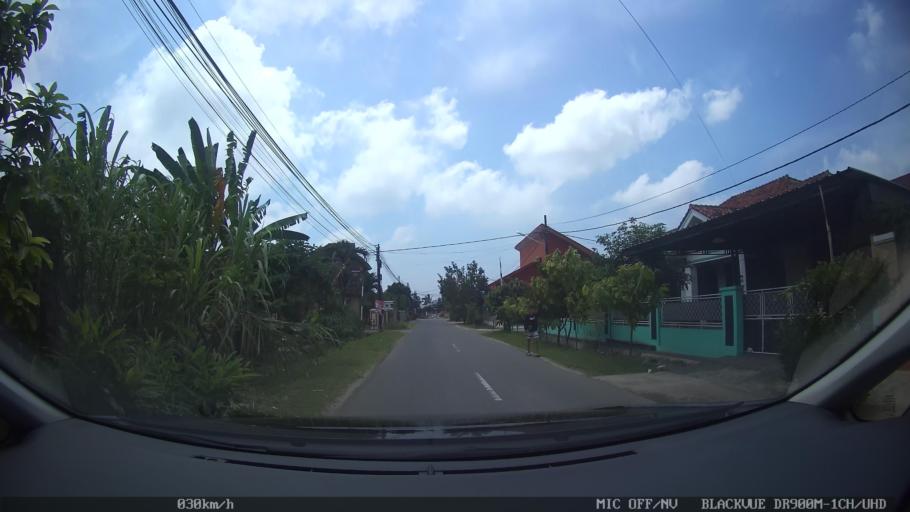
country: ID
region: Lampung
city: Kedaton
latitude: -5.3666
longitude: 105.3032
